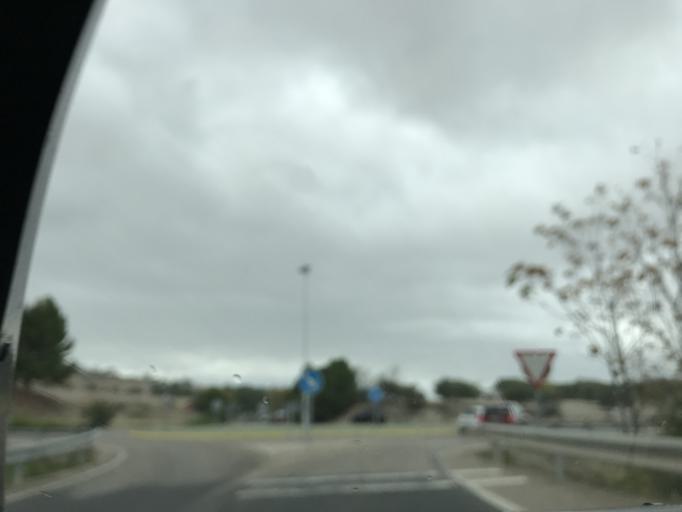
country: ES
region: Andalusia
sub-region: Provincia de Jaen
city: Peal de Becerro
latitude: 37.9197
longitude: -3.1214
